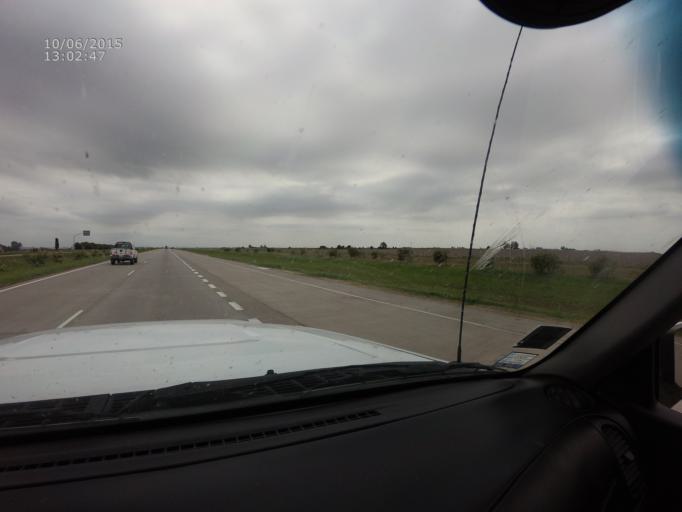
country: AR
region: Santa Fe
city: Armstrong
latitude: -32.7847
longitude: -61.7492
